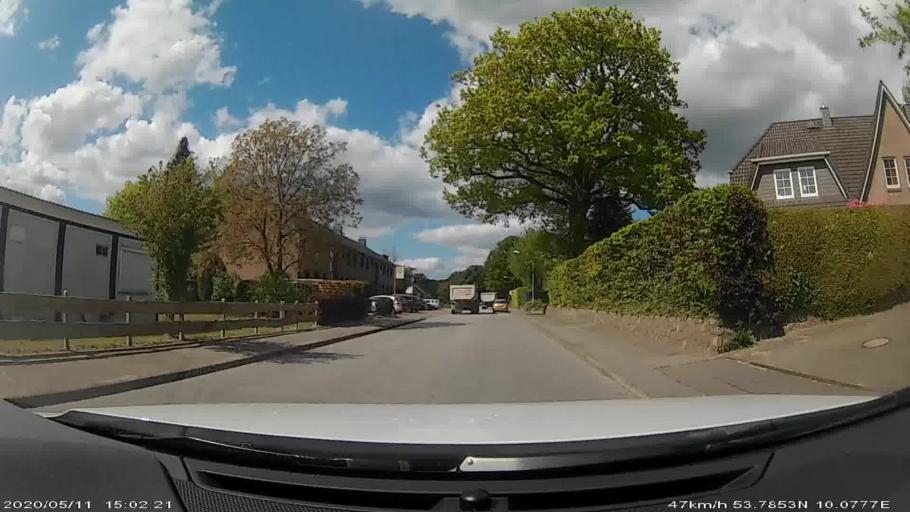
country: DE
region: Schleswig-Holstein
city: Huttblek
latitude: 53.7904
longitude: 10.0586
